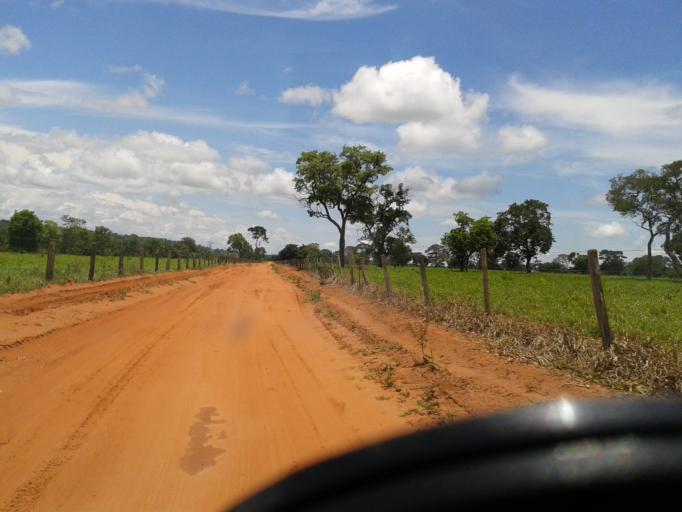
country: BR
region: Minas Gerais
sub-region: Santa Vitoria
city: Santa Vitoria
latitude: -18.9420
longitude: -49.8607
